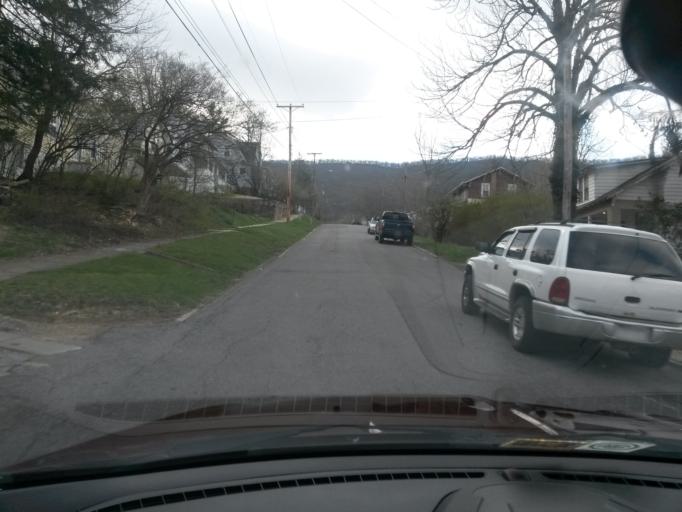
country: US
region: West Virginia
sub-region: Mercer County
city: Bluefield
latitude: 37.2525
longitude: -81.2163
